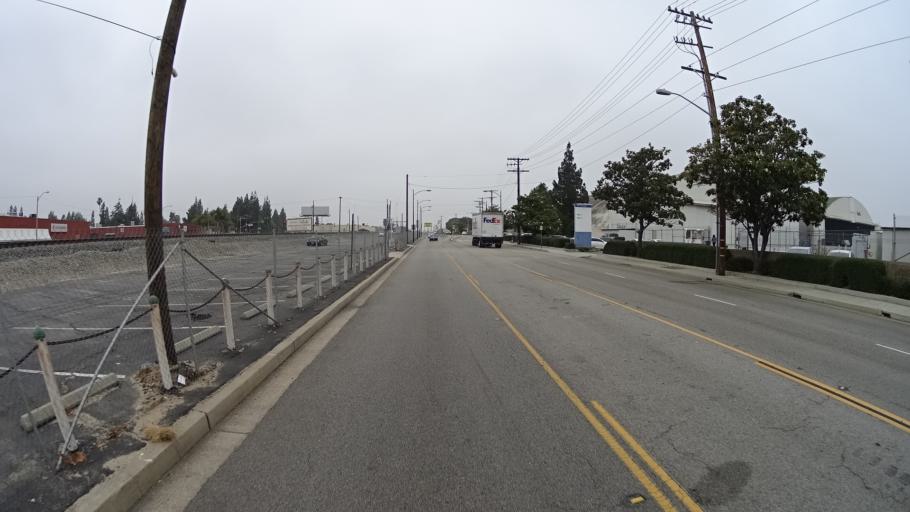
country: US
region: California
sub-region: Los Angeles County
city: North Hollywood
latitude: 34.1942
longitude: -118.3593
